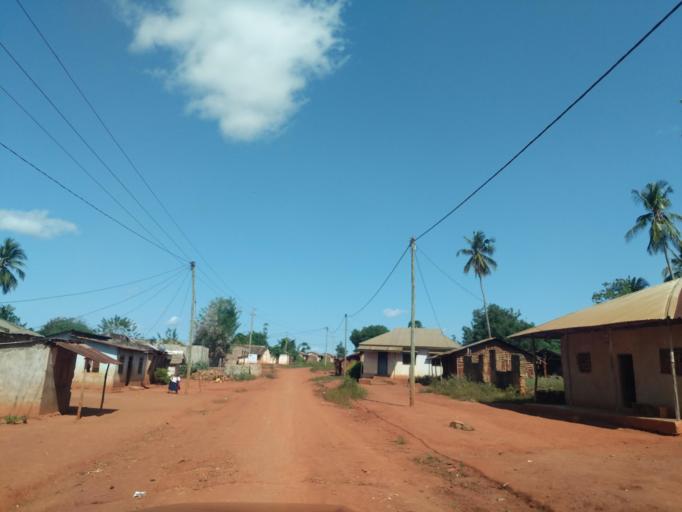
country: TZ
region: Tanga
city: Muheza
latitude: -5.3863
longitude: 38.5772
